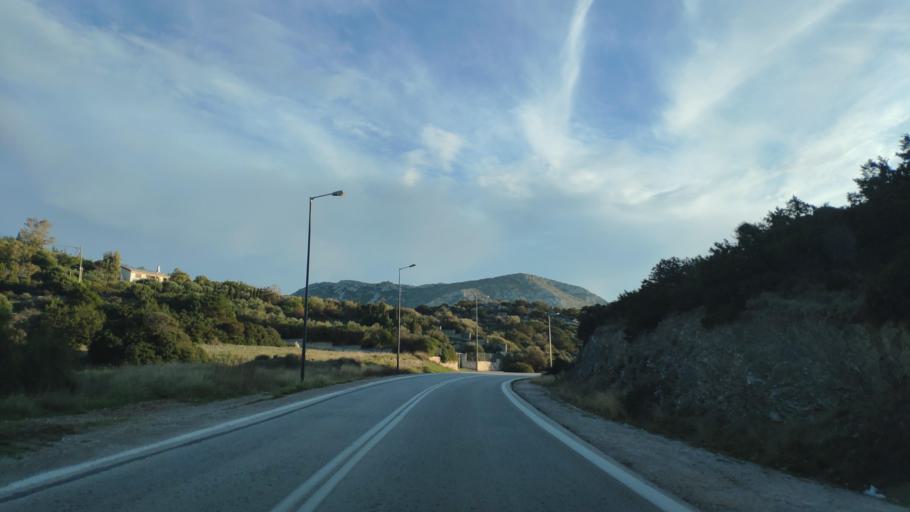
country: GR
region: Attica
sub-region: Nomarchia Anatolikis Attikis
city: Palaia Fokaia
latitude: 37.6867
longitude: 23.9382
